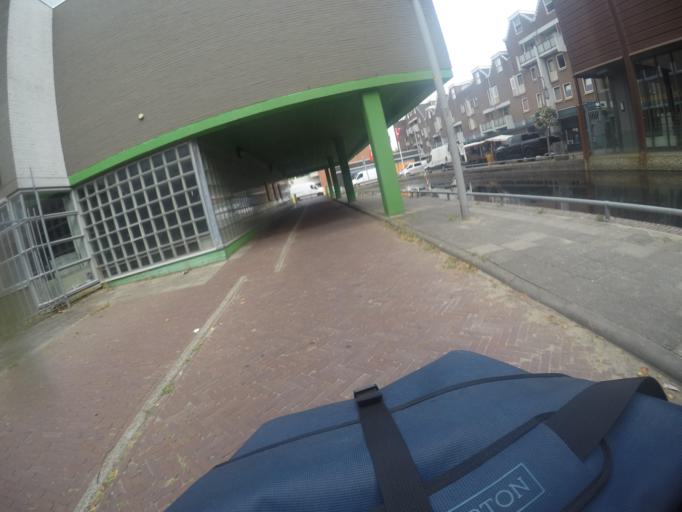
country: NL
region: Flevoland
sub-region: Gemeente Almere
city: Almere Stad
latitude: 52.3366
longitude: 5.2178
